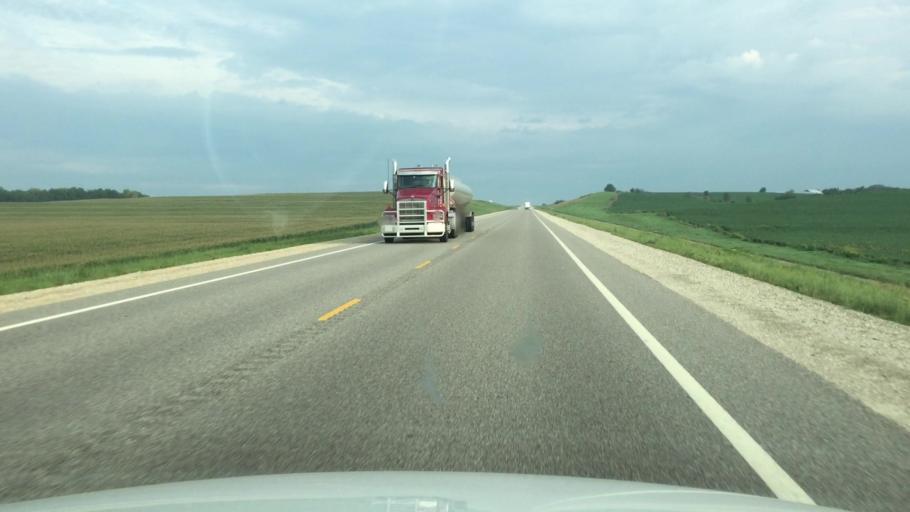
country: US
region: Kansas
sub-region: Doniphan County
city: Highland
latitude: 39.8195
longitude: -95.2093
